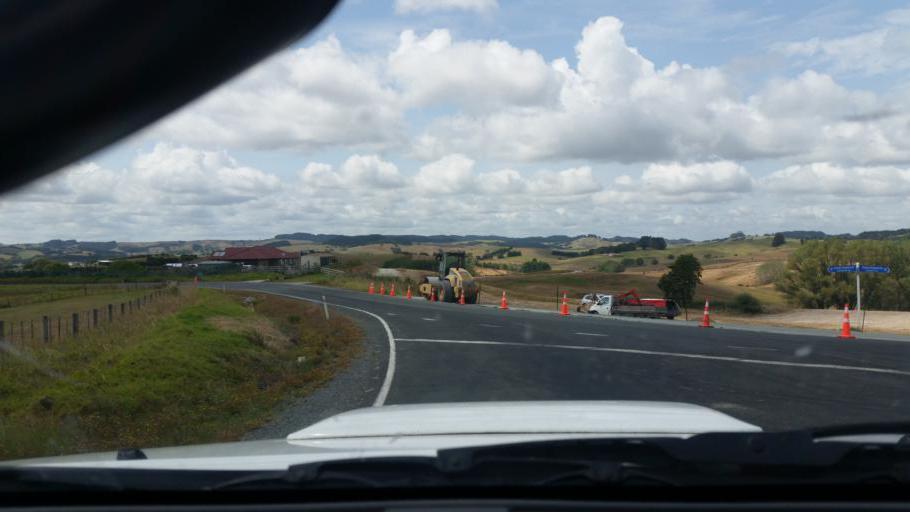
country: NZ
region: Auckland
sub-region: Auckland
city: Wellsford
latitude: -36.1440
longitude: 174.4884
